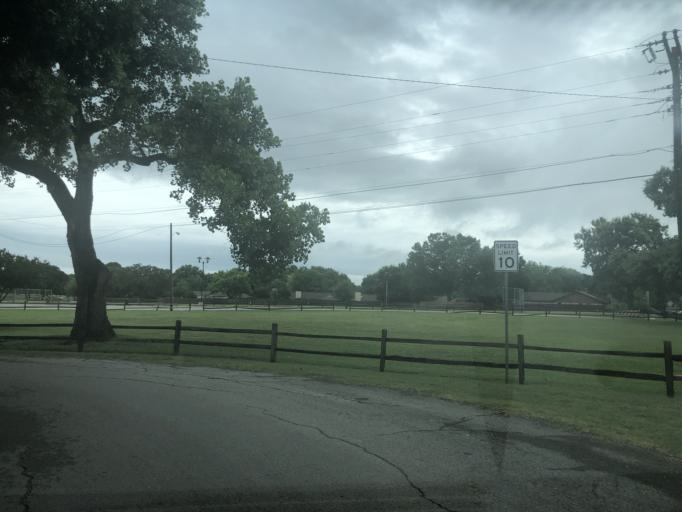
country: US
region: Texas
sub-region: Dallas County
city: Irving
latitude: 32.7975
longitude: -96.9430
